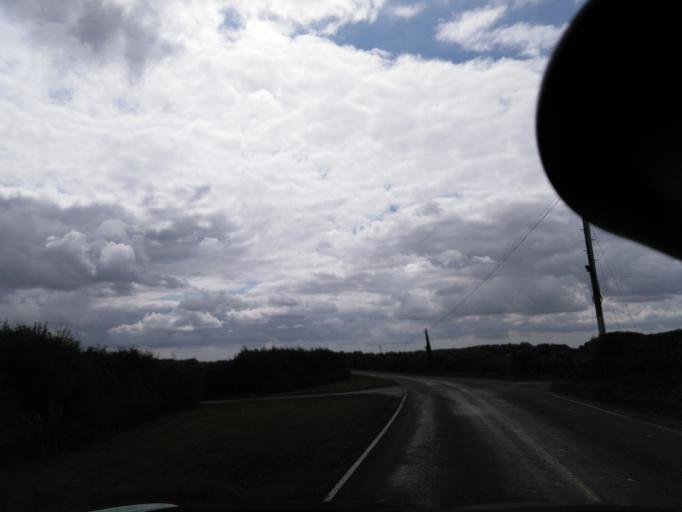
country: GB
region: England
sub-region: Dorset
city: Shaftesbury
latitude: 50.9440
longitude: -2.1644
